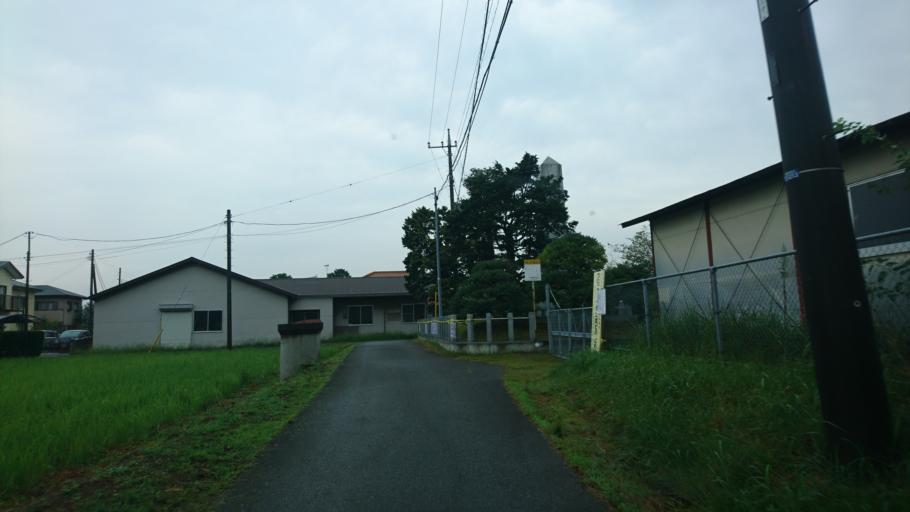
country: JP
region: Chiba
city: Kimitsu
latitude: 35.2906
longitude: 139.9863
